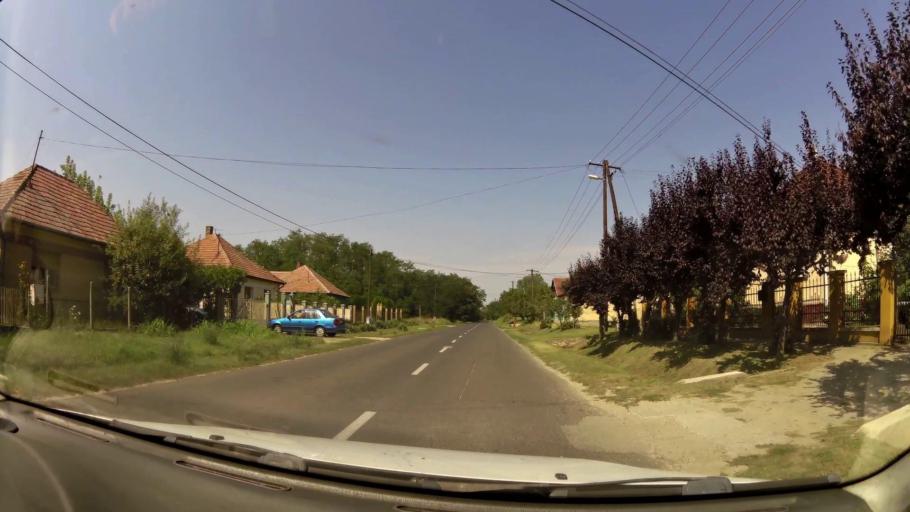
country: HU
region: Pest
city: Tapiosag
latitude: 47.4079
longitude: 19.6168
